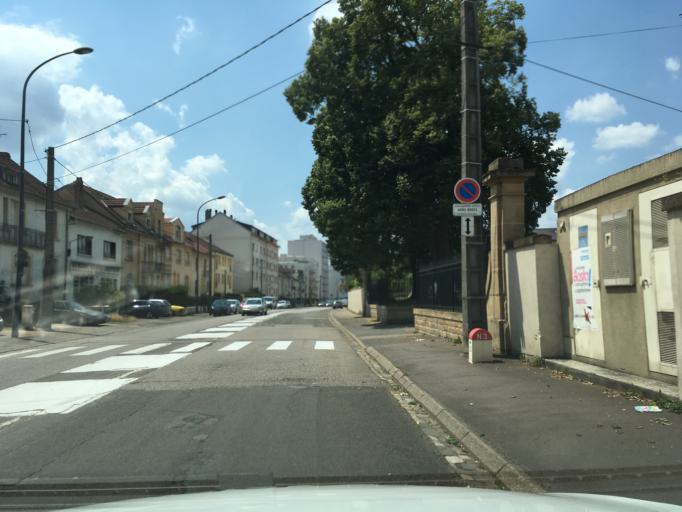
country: FR
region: Lorraine
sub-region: Departement de la Moselle
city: Saint-Julien-les-Metz
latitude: 49.1199
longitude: 6.2078
